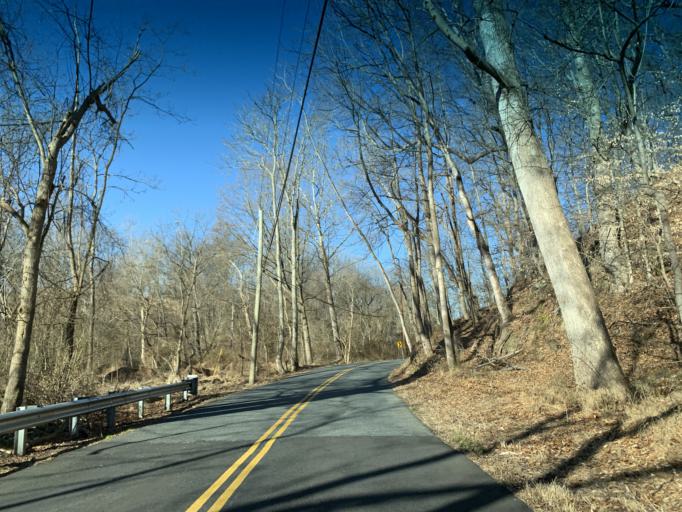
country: US
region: Maryland
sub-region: Harford County
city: South Bel Air
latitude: 39.6292
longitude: -76.2938
